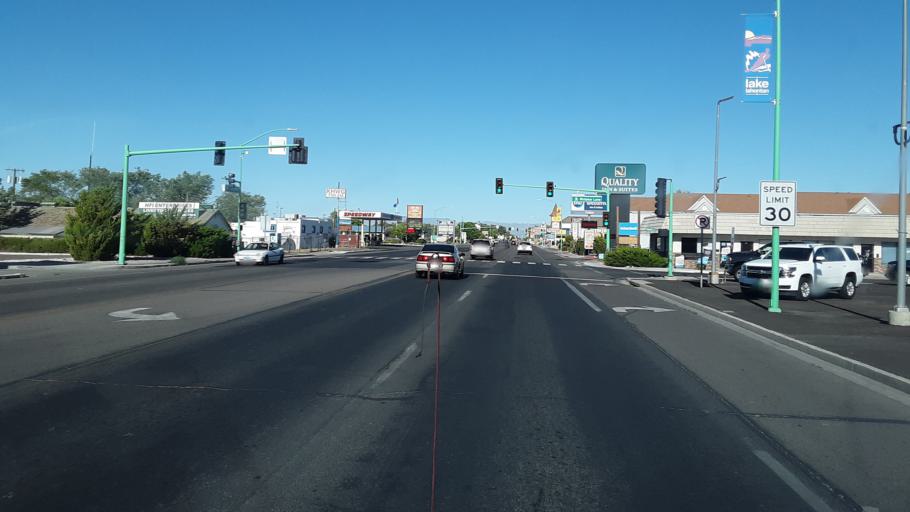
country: US
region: Nevada
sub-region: Churchill County
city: Fallon
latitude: 39.4749
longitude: -118.7913
